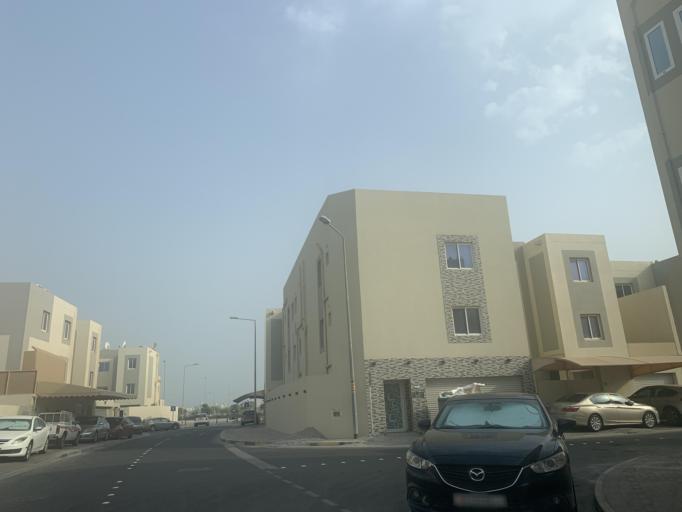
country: BH
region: Manama
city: Jidd Hafs
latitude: 26.2276
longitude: 50.4530
